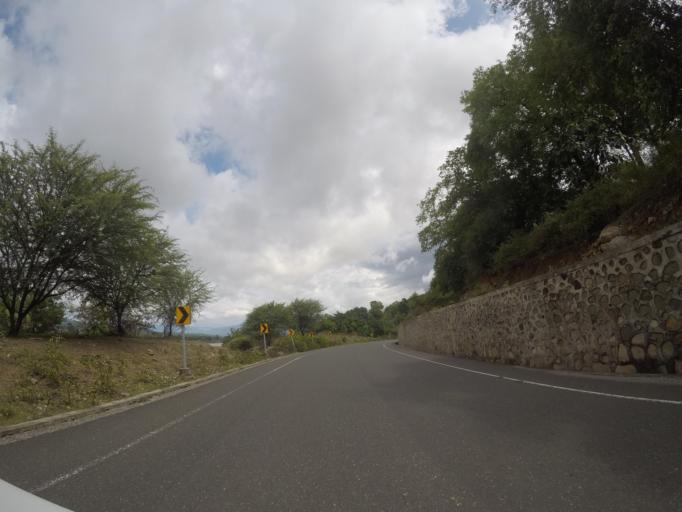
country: TL
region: Liquica
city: Maubara
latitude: -8.7430
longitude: 125.1252
